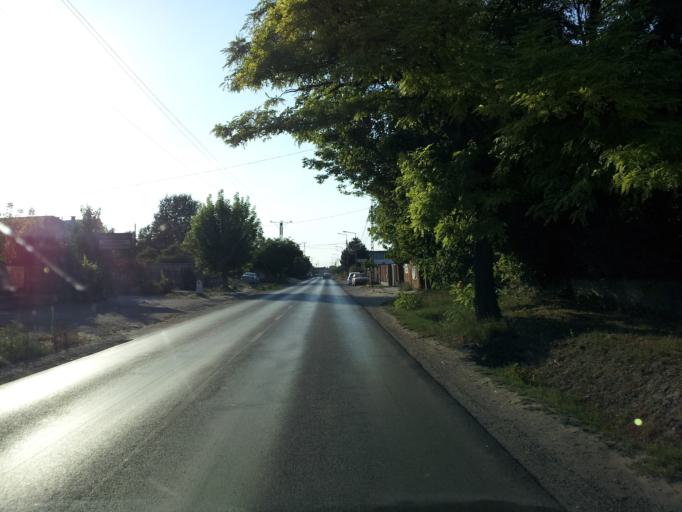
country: HU
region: Pest
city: Szigethalom
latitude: 47.3197
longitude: 19.0186
